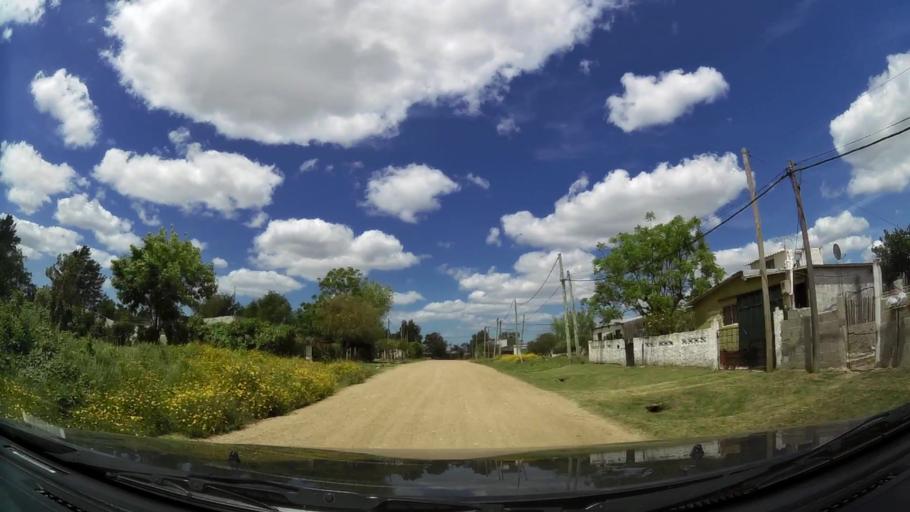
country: UY
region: Canelones
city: Colonia Nicolich
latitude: -34.7934
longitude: -55.9959
